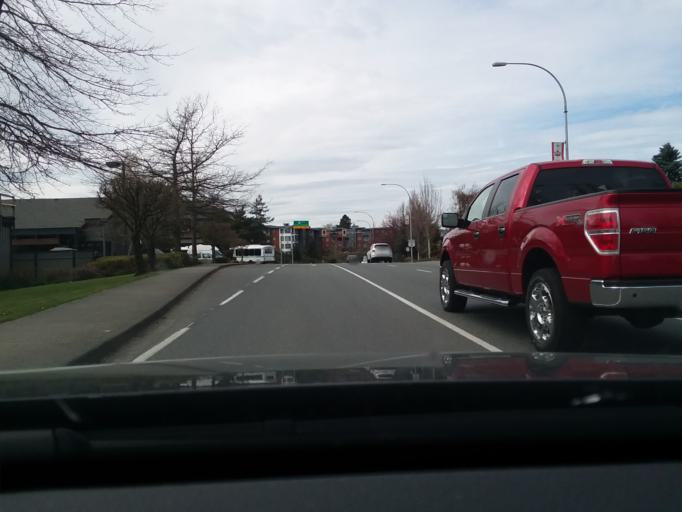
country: CA
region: British Columbia
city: Victoria
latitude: 48.4588
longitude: -123.3766
